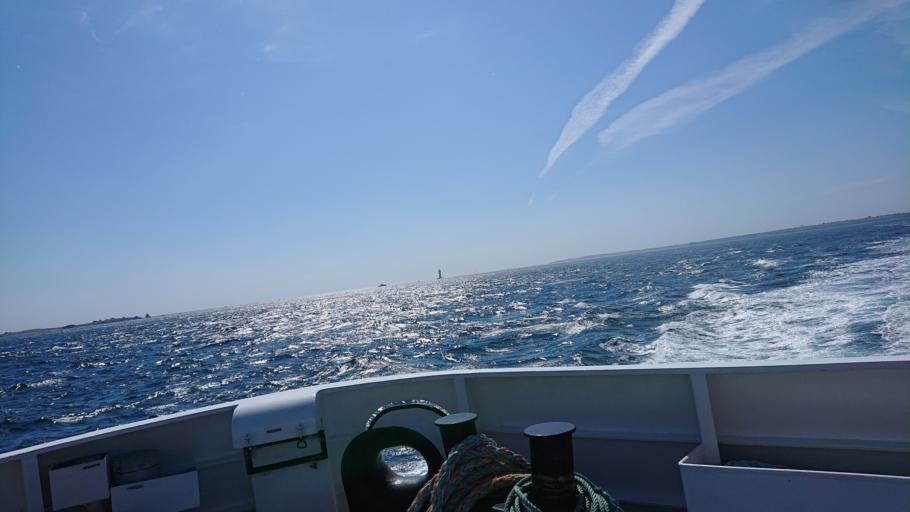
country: FR
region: Brittany
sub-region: Departement du Finistere
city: Lampaul-Plouarzel
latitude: 48.4443
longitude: -4.9906
